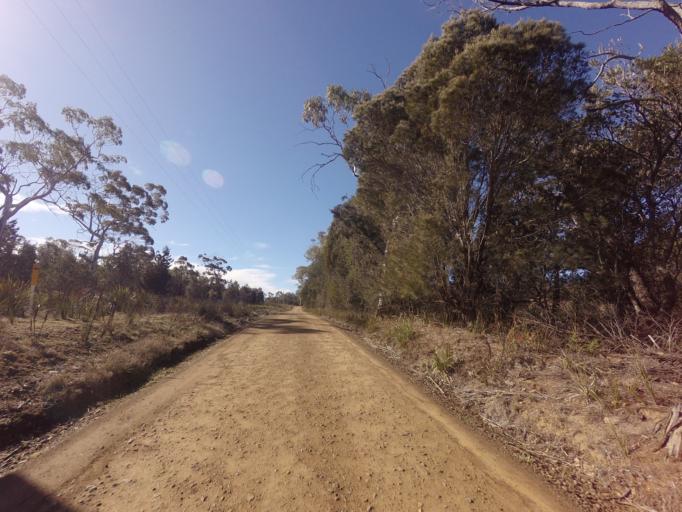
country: AU
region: Tasmania
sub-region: Sorell
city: Sorell
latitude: -42.3553
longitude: 147.9658
